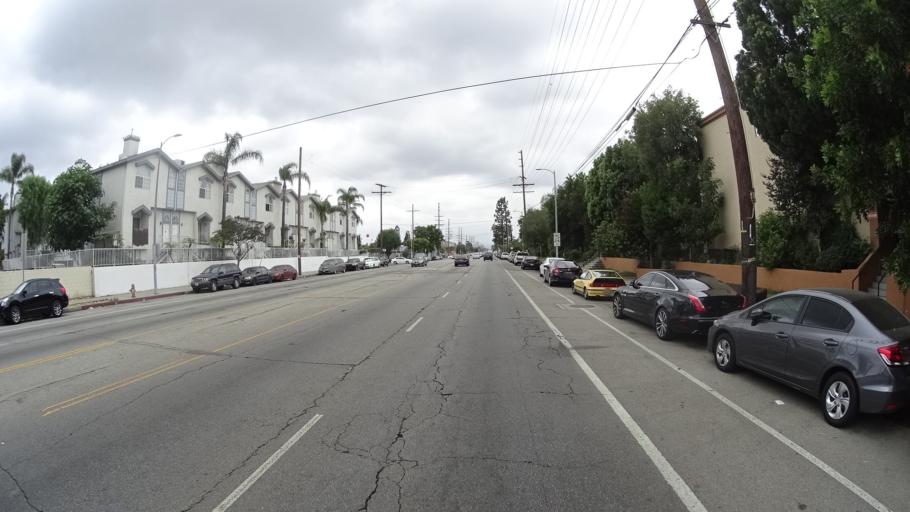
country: US
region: California
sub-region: Los Angeles County
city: San Fernando
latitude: 34.2356
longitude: -118.4548
